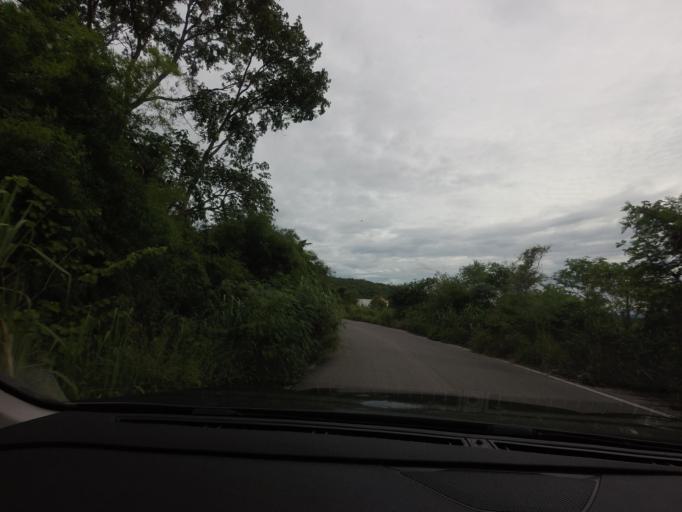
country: TH
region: Prachuap Khiri Khan
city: Hua Hin
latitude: 12.4883
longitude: 99.9421
